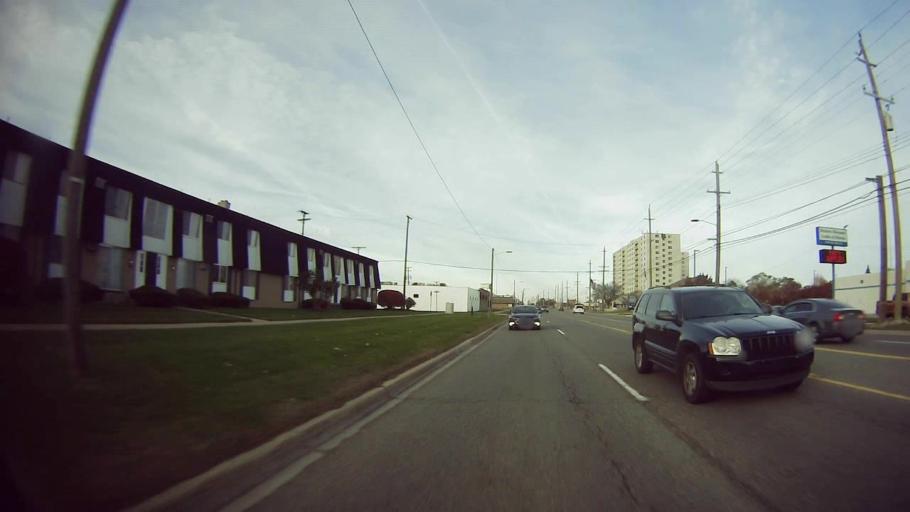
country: US
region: Michigan
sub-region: Macomb County
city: Warren
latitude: 42.4774
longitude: -83.0257
